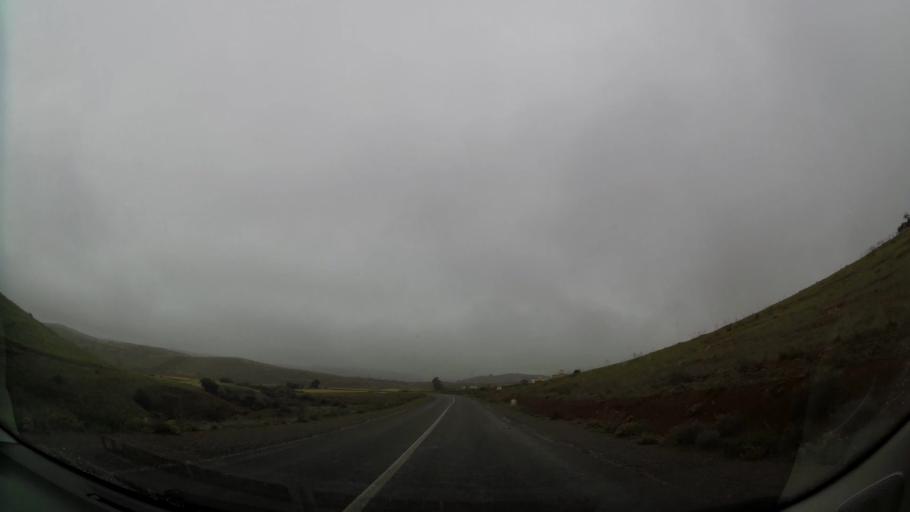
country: MA
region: Oriental
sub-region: Nador
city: Boudinar
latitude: 35.1095
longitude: -3.5705
